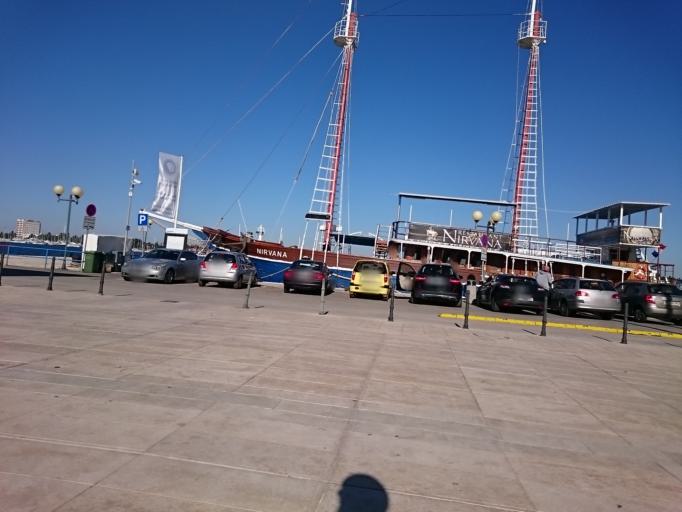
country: HR
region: Istarska
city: Umag
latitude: 45.4338
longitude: 13.5183
